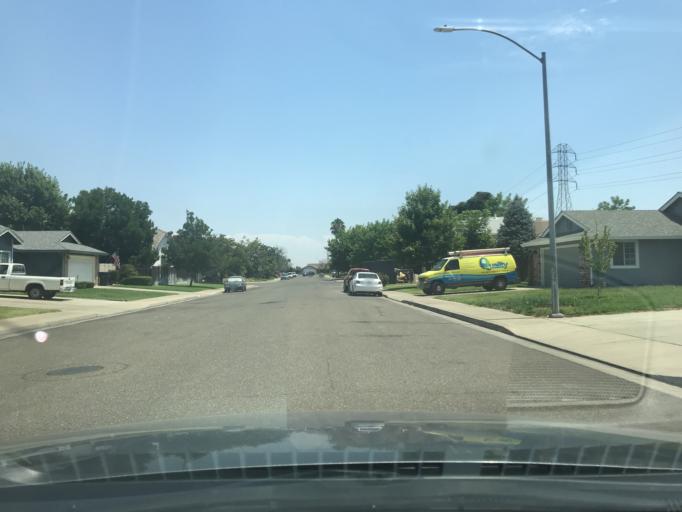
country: US
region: California
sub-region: Merced County
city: Atwater
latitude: 37.3681
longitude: -120.5942
